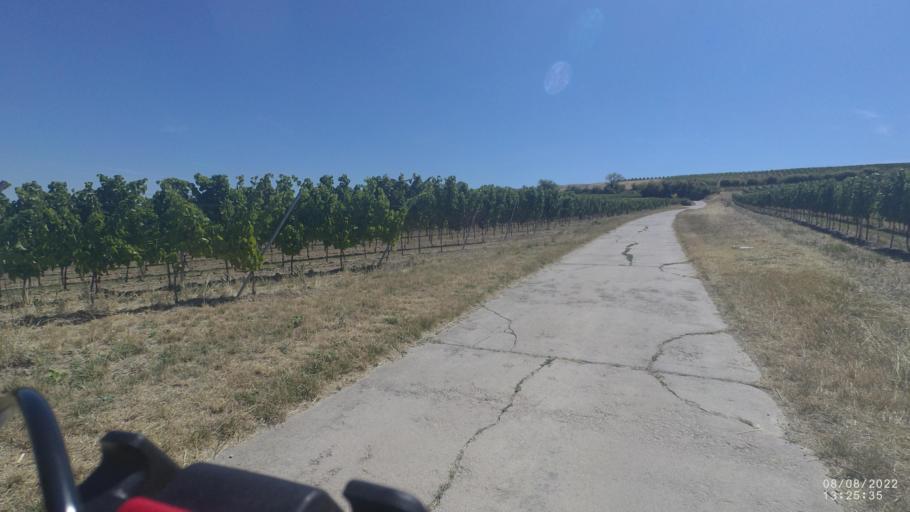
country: DE
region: Rheinland-Pfalz
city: Partenheim
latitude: 49.8766
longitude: 8.0893
